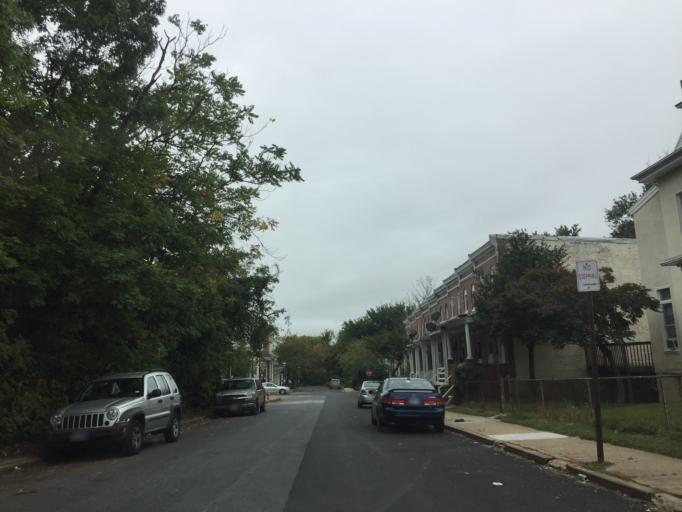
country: US
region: Maryland
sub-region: City of Baltimore
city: Baltimore
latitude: 39.3258
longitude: -76.6047
